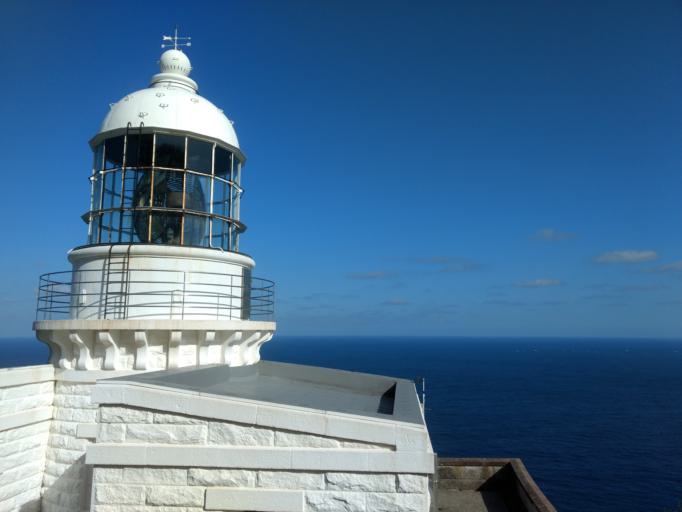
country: JP
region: Kyoto
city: Miyazu
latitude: 35.7767
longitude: 135.2234
